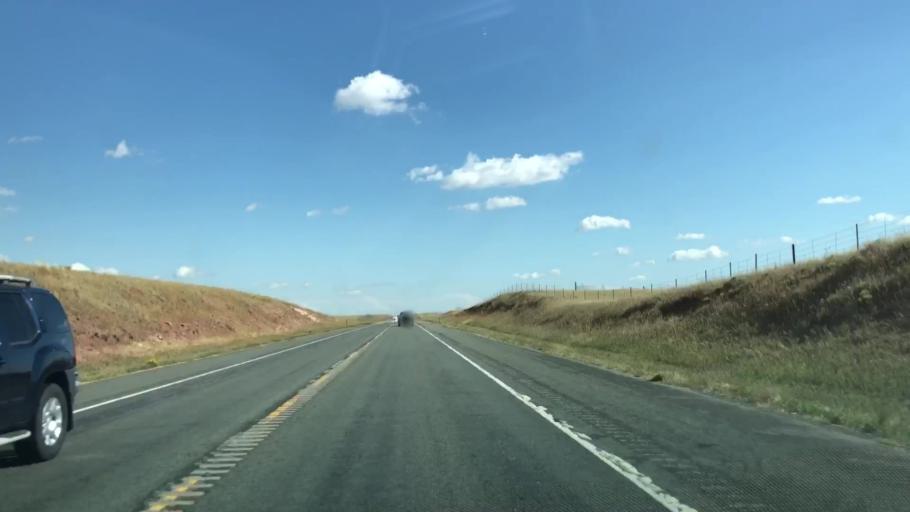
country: US
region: Colorado
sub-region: Larimer County
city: Laporte
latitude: 40.9185
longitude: -105.3242
